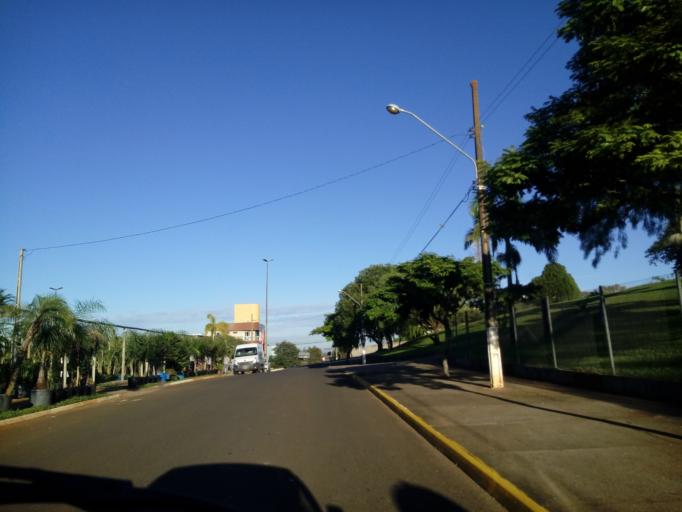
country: BR
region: Santa Catarina
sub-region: Chapeco
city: Chapeco
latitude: -27.1138
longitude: -52.6108
